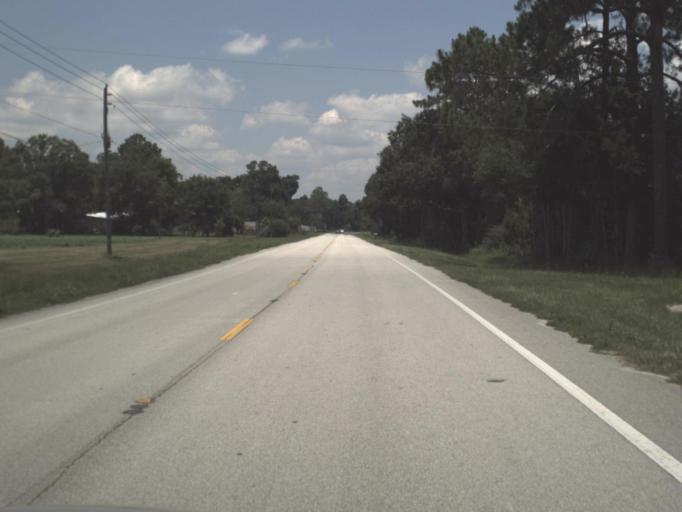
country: US
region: Florida
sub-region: Bradford County
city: Starke
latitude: 30.0168
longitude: -82.1475
